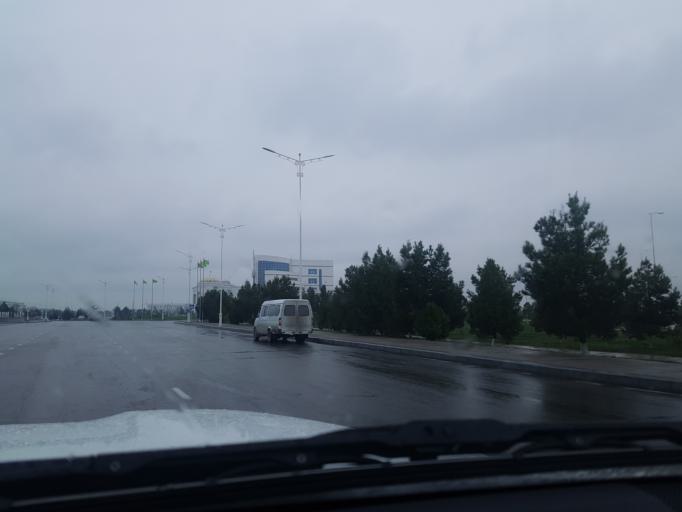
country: TM
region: Lebap
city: Turkmenabat
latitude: 39.0538
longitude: 63.5881
